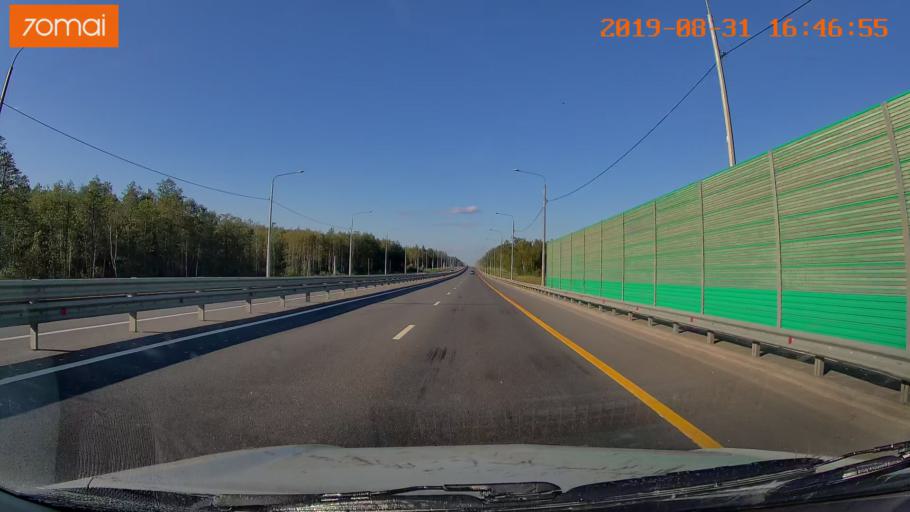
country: RU
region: Kaluga
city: Mstikhino
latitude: 54.6435
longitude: 36.1341
